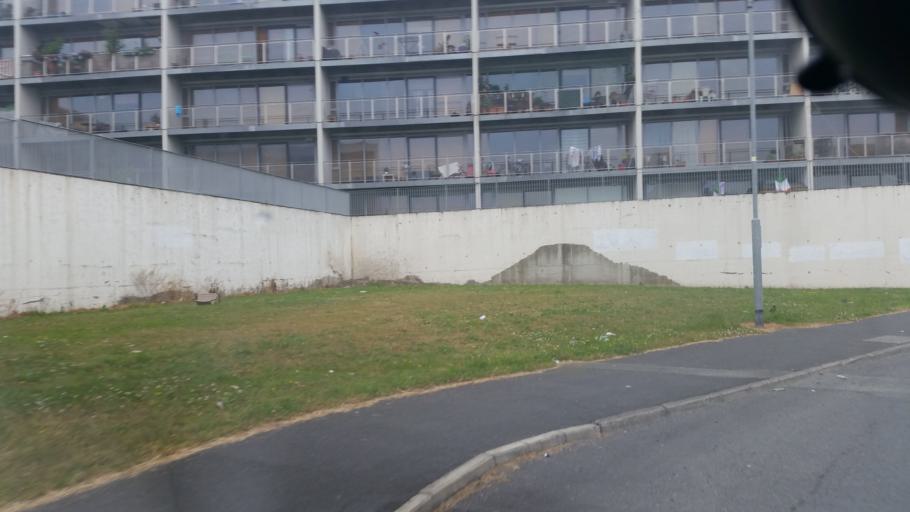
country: IE
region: Leinster
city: Ballymun
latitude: 53.4002
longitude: -6.2658
